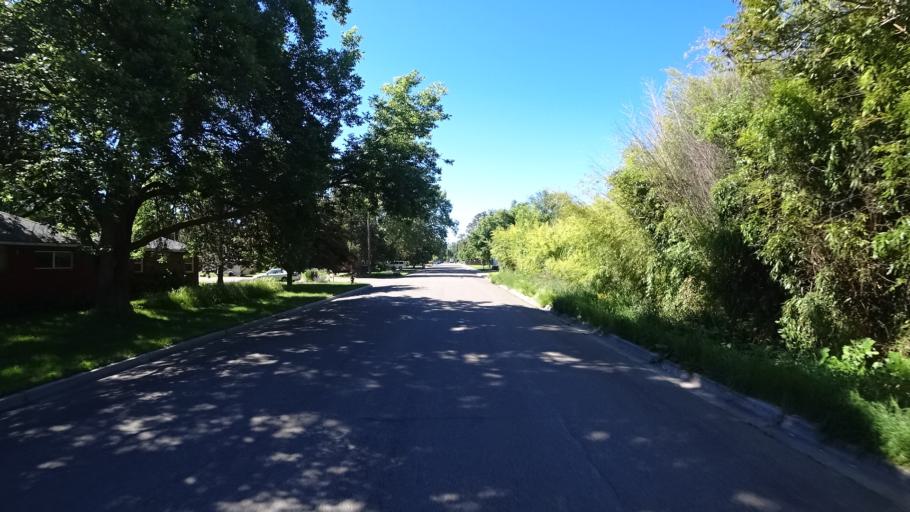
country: US
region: Idaho
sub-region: Ada County
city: Garden City
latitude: 43.6449
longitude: -116.2284
